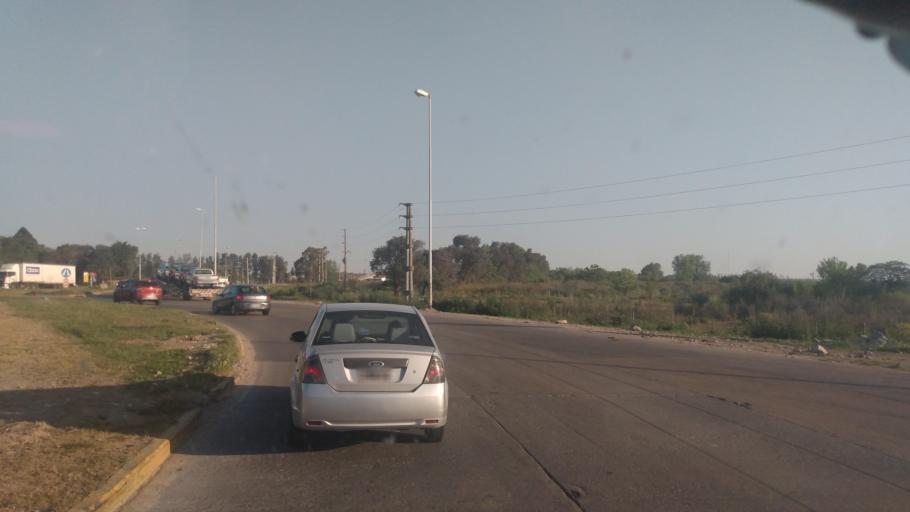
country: AR
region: Buenos Aires
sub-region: Partido de Campana
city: Campana
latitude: -34.2028
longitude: -58.9604
